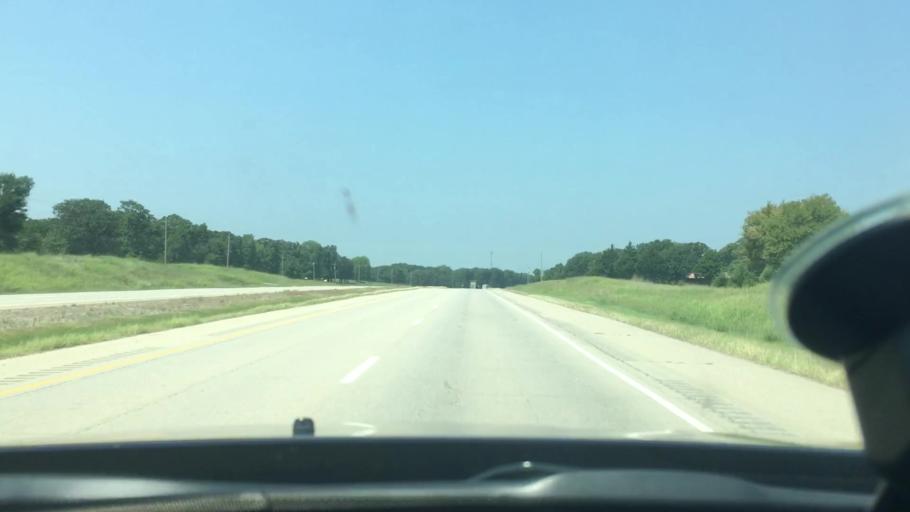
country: US
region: Oklahoma
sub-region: Atoka County
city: Atoka
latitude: 34.3143
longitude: -96.0257
